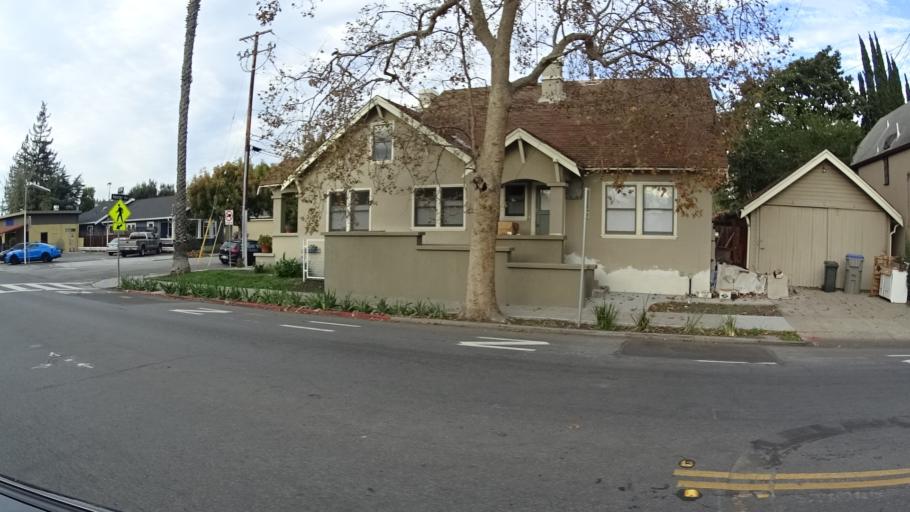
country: US
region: California
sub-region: Santa Clara County
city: Buena Vista
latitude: 37.3297
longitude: -121.9191
